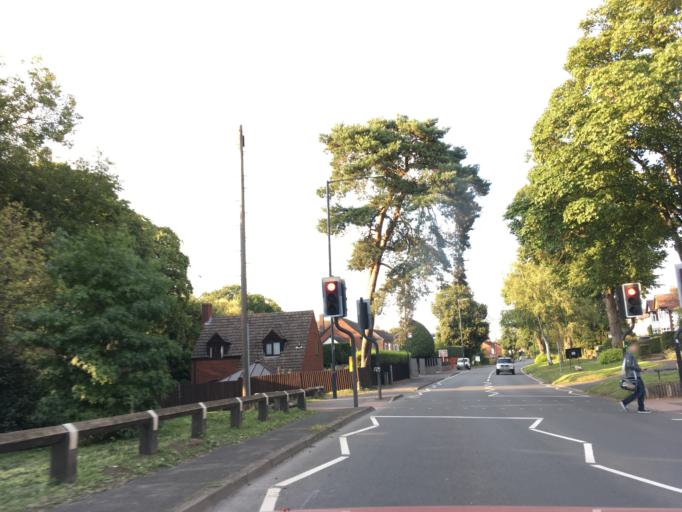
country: GB
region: England
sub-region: Warwickshire
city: Stratford-upon-Avon
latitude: 52.1847
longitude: -1.7004
